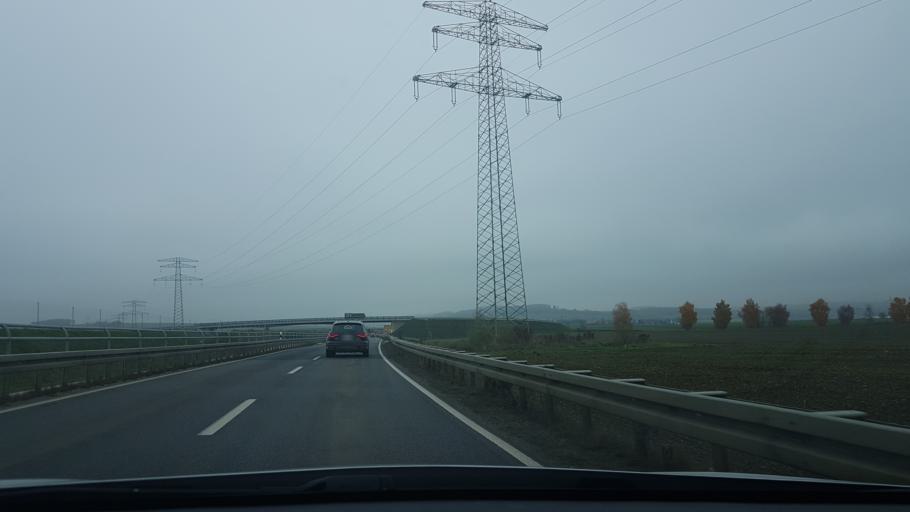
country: DE
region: Bavaria
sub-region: Lower Bavaria
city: Essenbach
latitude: 48.6085
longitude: 12.2306
